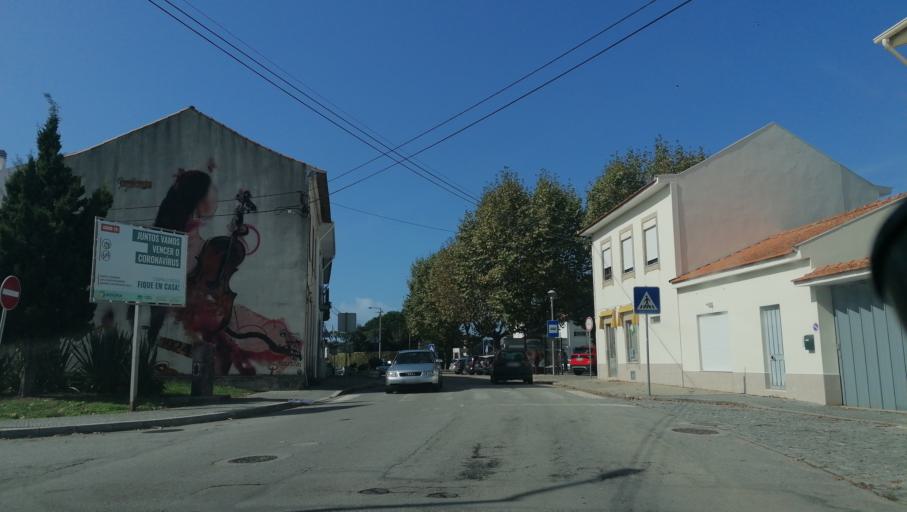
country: PT
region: Aveiro
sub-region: Espinho
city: Silvalde
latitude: 41.0057
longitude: -8.6243
